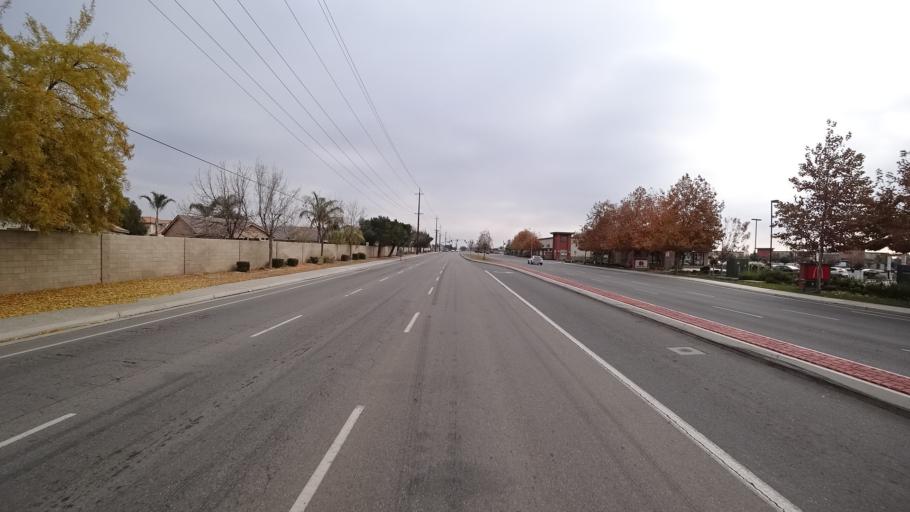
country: US
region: California
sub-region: Kern County
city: Greenfield
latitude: 35.2961
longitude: -119.0771
